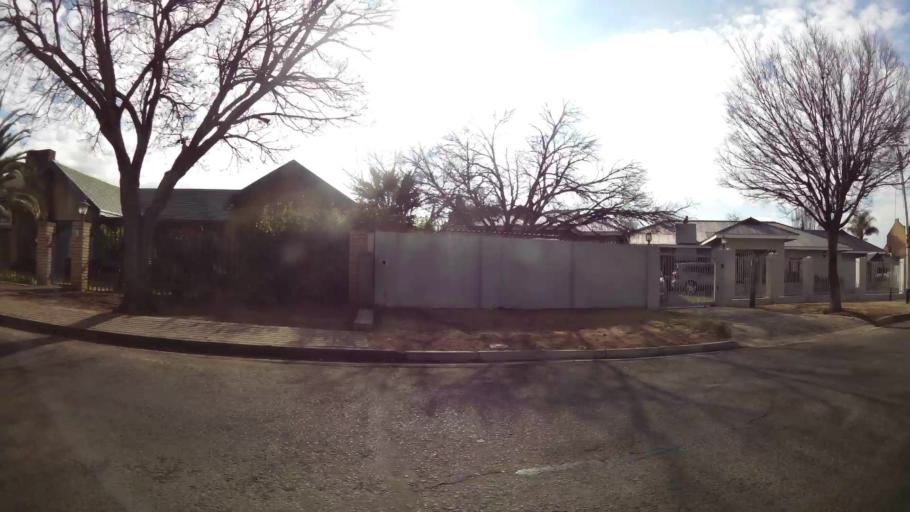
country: ZA
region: Orange Free State
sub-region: Mangaung Metropolitan Municipality
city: Bloemfontein
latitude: -29.0784
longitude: 26.2117
